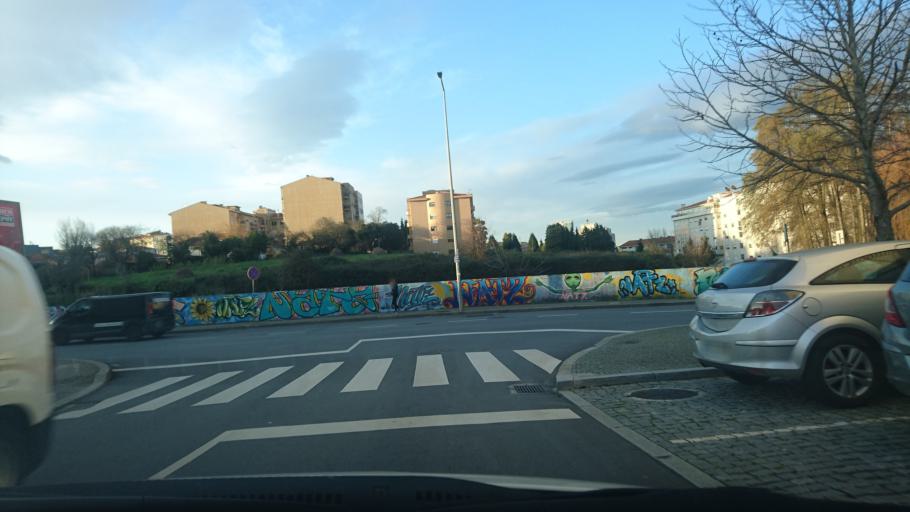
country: PT
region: Porto
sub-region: Vila Nova de Gaia
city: Vila Nova de Gaia
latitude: 41.1221
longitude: -8.6244
